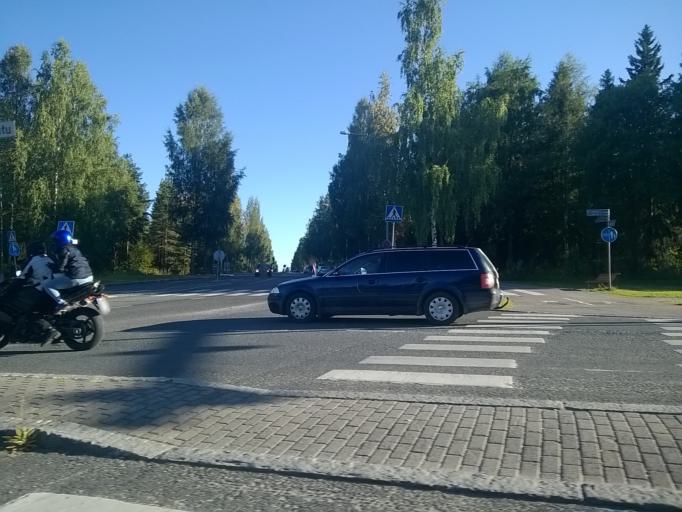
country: FI
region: Pirkanmaa
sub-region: Tampere
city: Tampere
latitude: 61.4582
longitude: 23.8445
